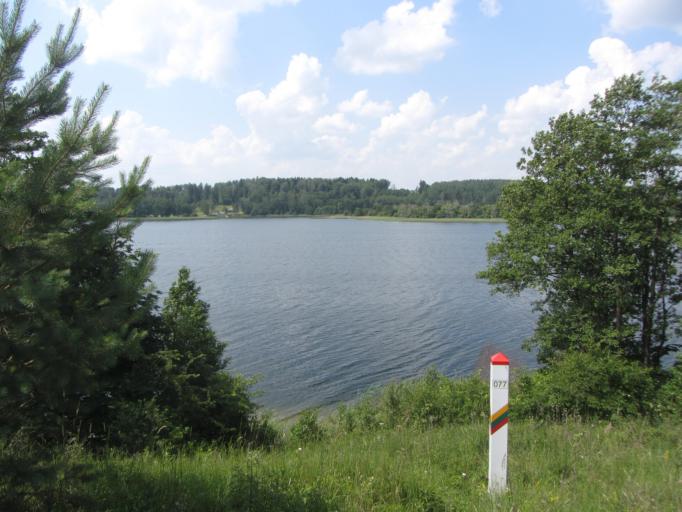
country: LT
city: Lazdijai
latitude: 54.1891
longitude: 23.4240
